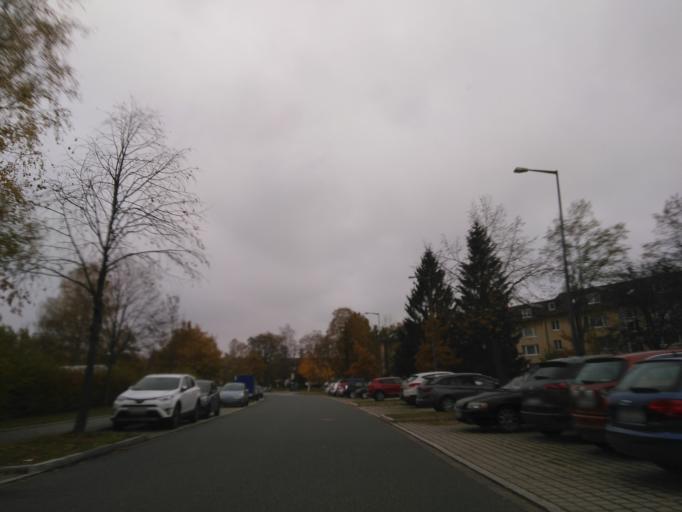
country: DE
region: Bavaria
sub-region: Upper Bavaria
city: Unterhaching
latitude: 48.0921
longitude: 11.5926
